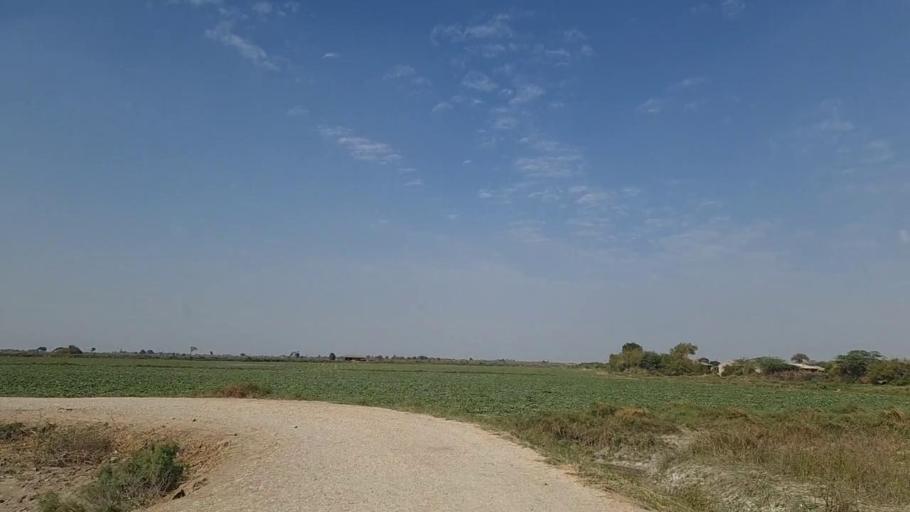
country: PK
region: Sindh
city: Jati
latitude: 24.4790
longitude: 68.2668
